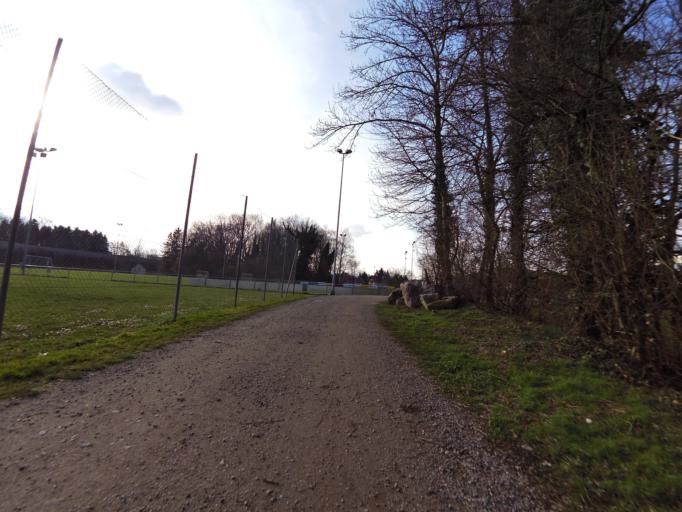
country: CH
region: Zurich
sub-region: Bezirk Dietikon
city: Oberengstringen
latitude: 47.4052
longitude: 8.4676
